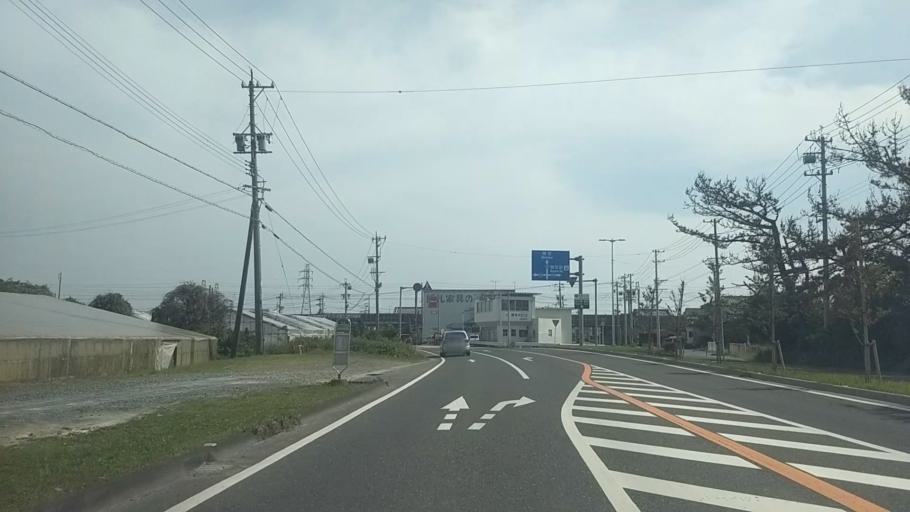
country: JP
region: Shizuoka
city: Kosai-shi
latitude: 34.6888
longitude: 137.6292
